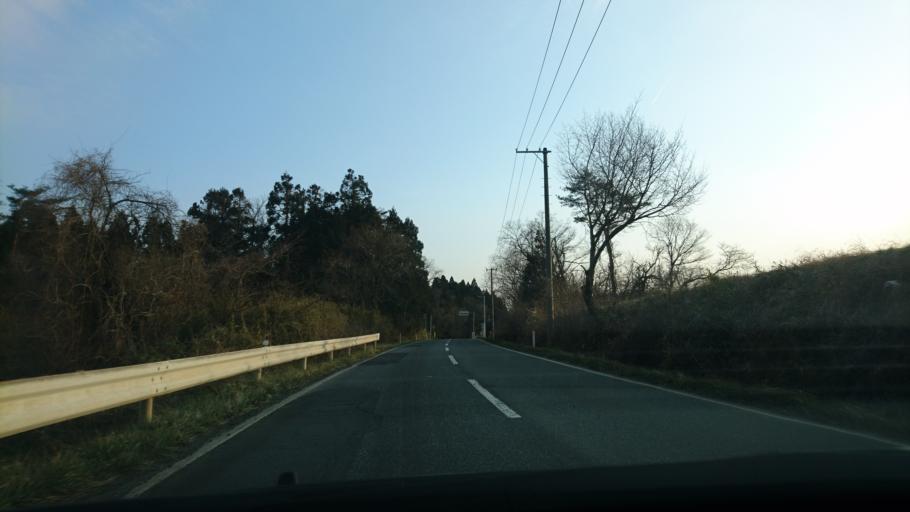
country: JP
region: Iwate
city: Ichinoseki
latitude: 38.8836
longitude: 141.2189
